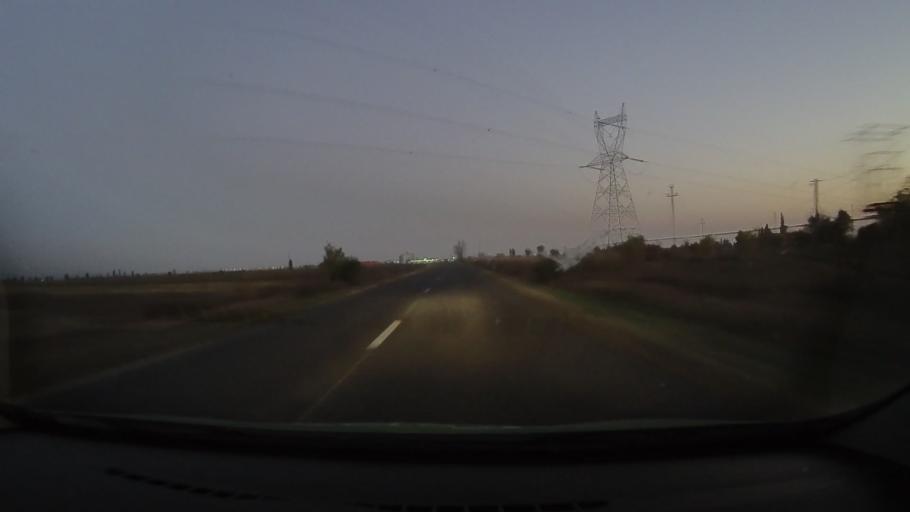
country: RO
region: Arad
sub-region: Comuna Livada
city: Livada
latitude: 46.1945
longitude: 21.3902
